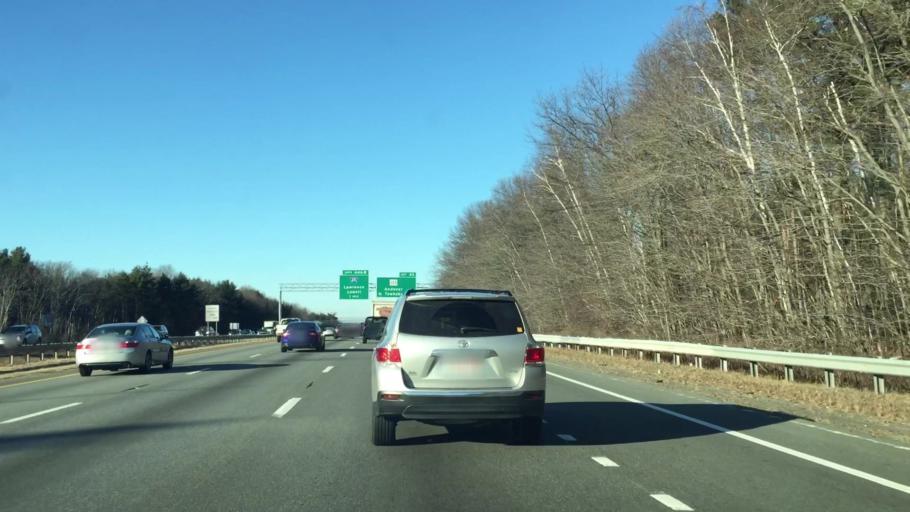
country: US
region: Massachusetts
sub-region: Essex County
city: Andover
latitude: 42.6420
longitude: -71.1840
